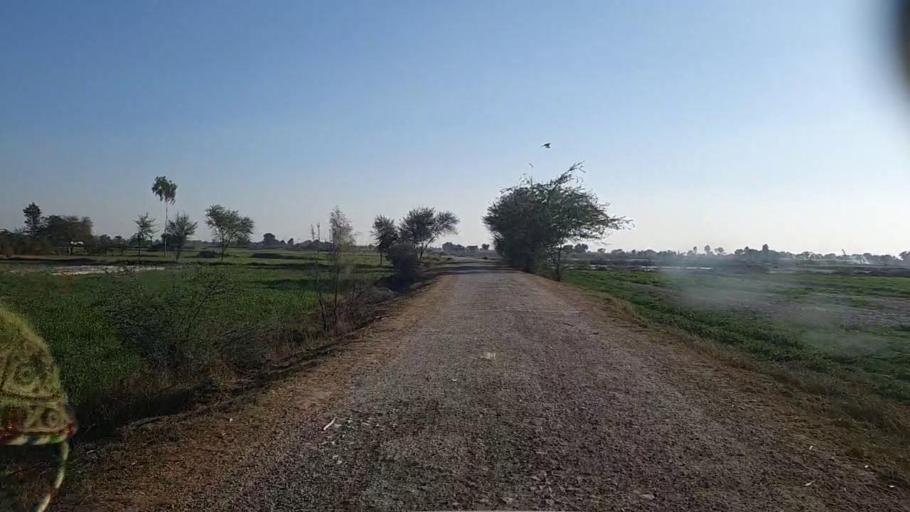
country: PK
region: Sindh
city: Khairpur
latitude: 28.0196
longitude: 69.7107
